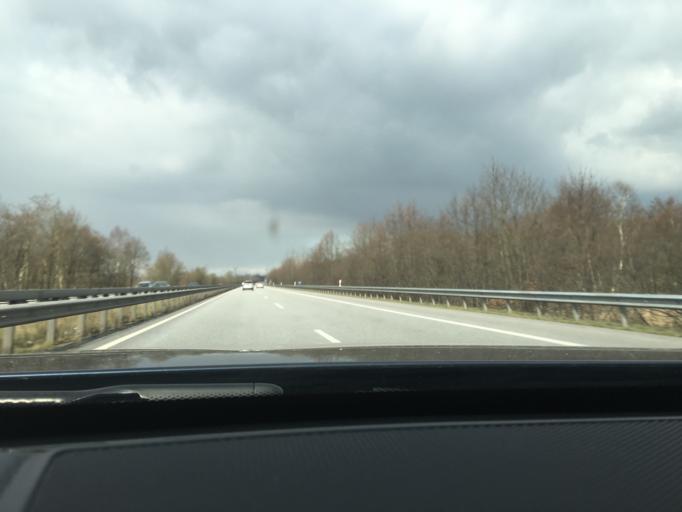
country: DE
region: Lower Saxony
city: Driftsethe
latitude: 53.4240
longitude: 8.5806
